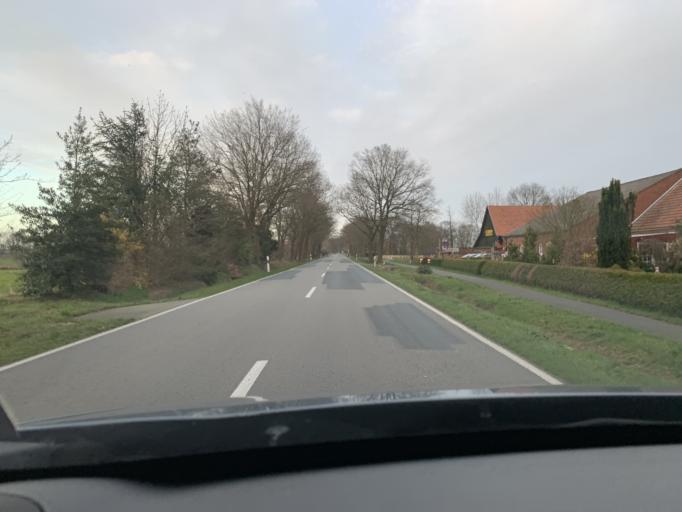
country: DE
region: Lower Saxony
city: Apen
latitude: 53.1836
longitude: 7.8452
